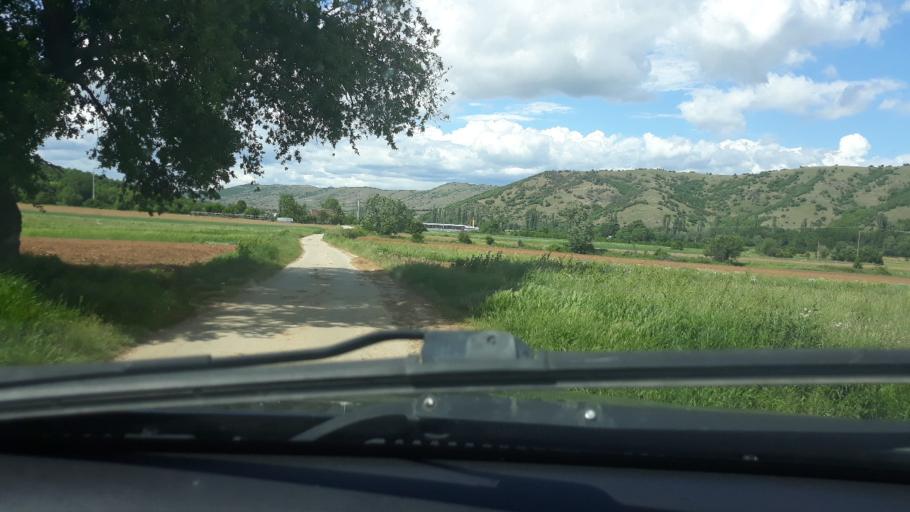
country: MK
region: Krivogastani
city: Krivogashtani
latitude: 41.3436
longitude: 21.2992
